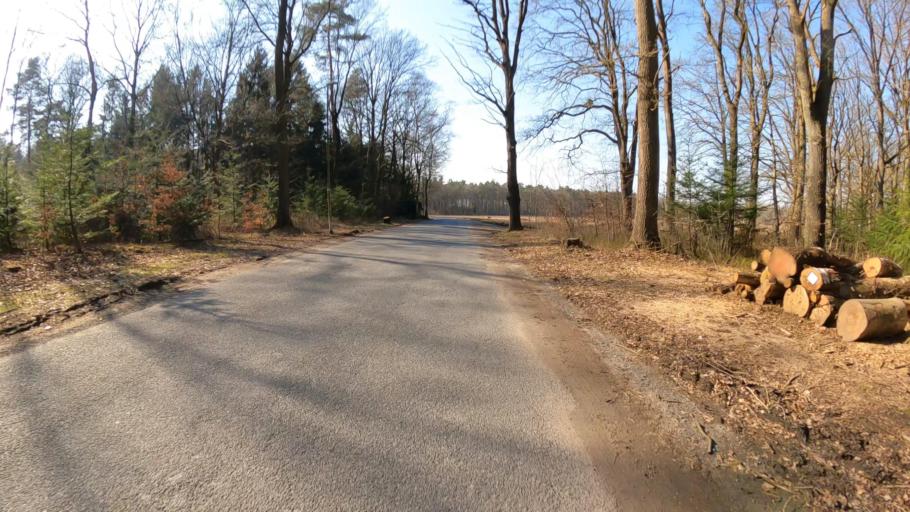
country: DE
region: Lower Saxony
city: Buchholz in der Nordheide
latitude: 53.3098
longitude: 9.8385
